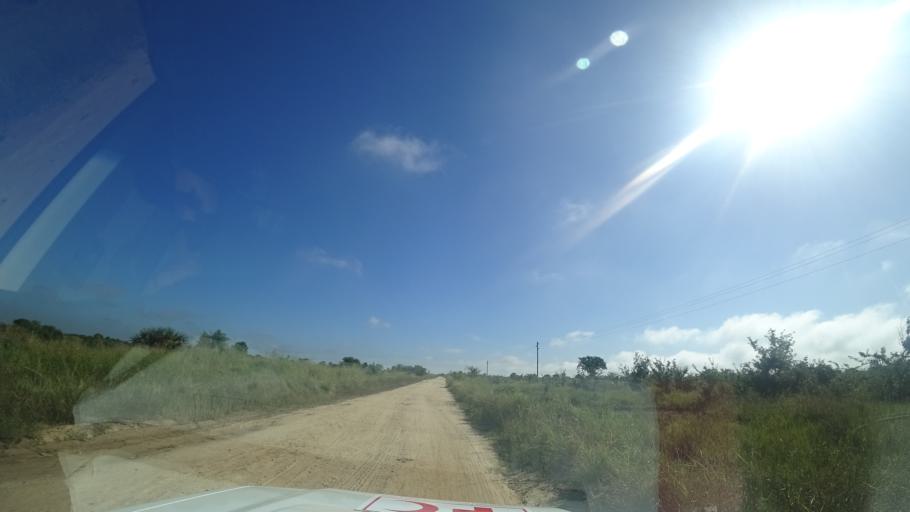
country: MZ
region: Sofala
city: Dondo
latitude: -19.4335
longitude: 34.5610
